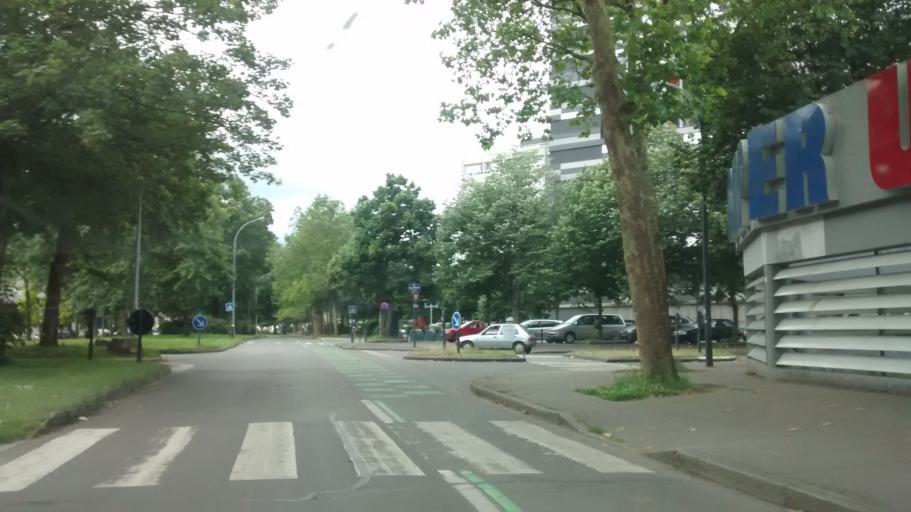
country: FR
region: Brittany
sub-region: Departement d'Ille-et-Vilaine
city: Rennes
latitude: 48.0911
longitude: -1.6798
